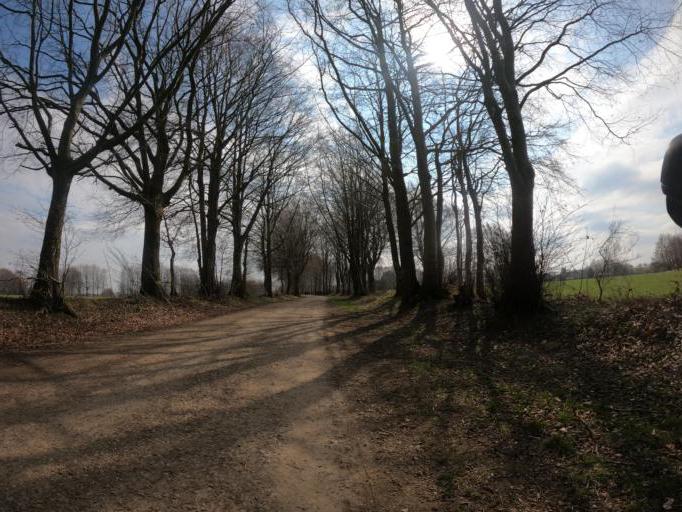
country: DE
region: North Rhine-Westphalia
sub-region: Regierungsbezirk Koln
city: Simmerath
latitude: 50.6039
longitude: 6.2857
